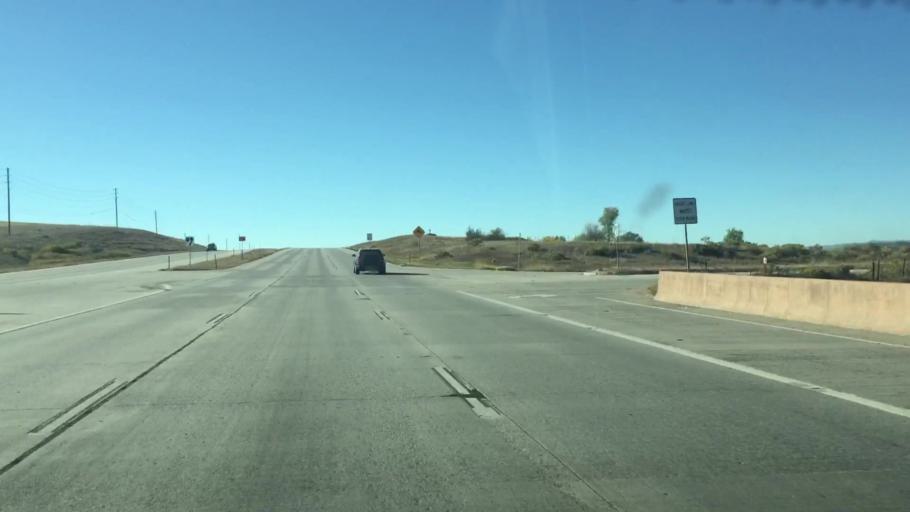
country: US
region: Colorado
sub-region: Douglas County
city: The Pinery
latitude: 39.4742
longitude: -104.7585
